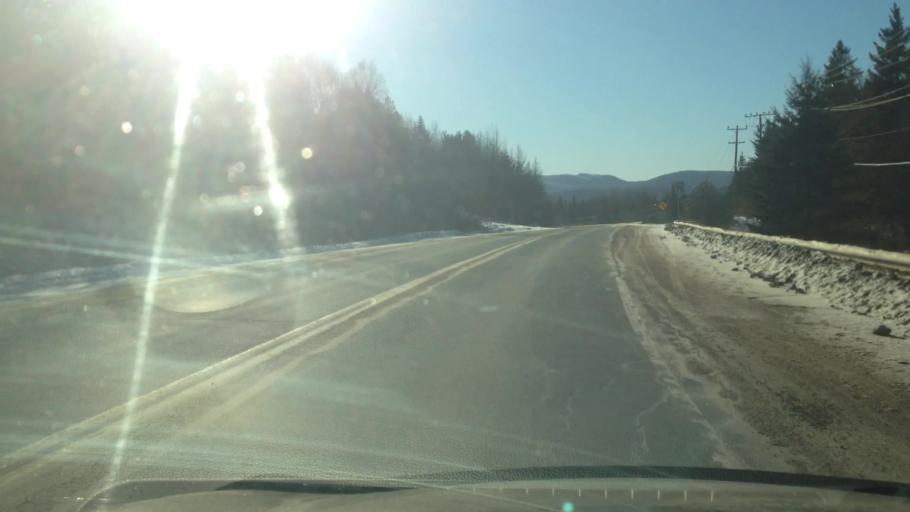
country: CA
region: Quebec
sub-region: Laurentides
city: Mont-Tremblant
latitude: 46.1088
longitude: -74.5985
